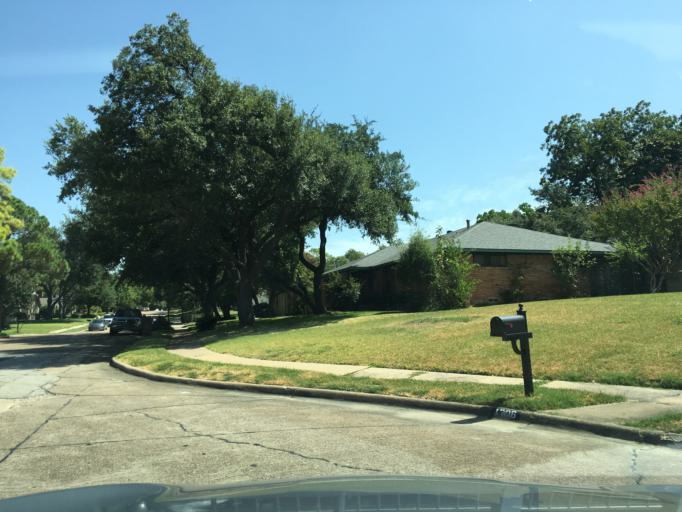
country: US
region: Texas
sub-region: Dallas County
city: Garland
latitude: 32.8730
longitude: -96.6093
